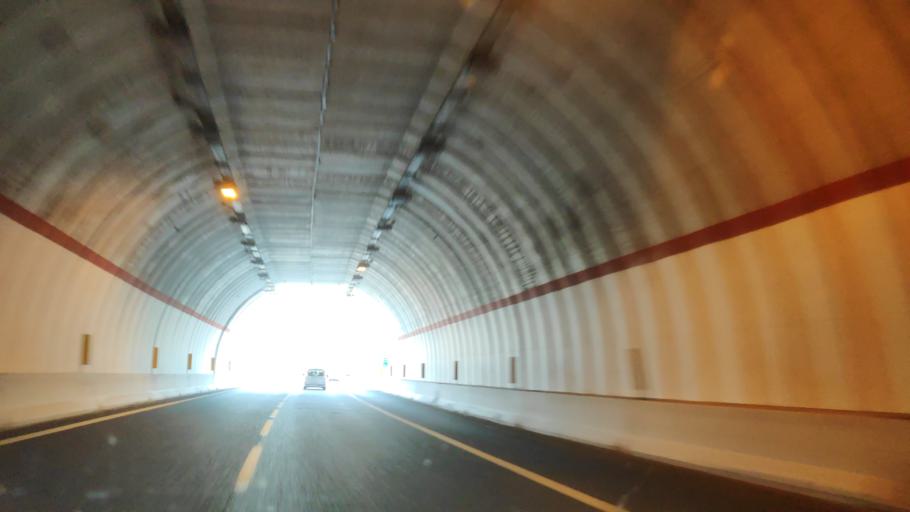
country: IT
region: Basilicate
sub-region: Provincia di Potenza
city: Lauria
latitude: 40.0301
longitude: 15.8750
